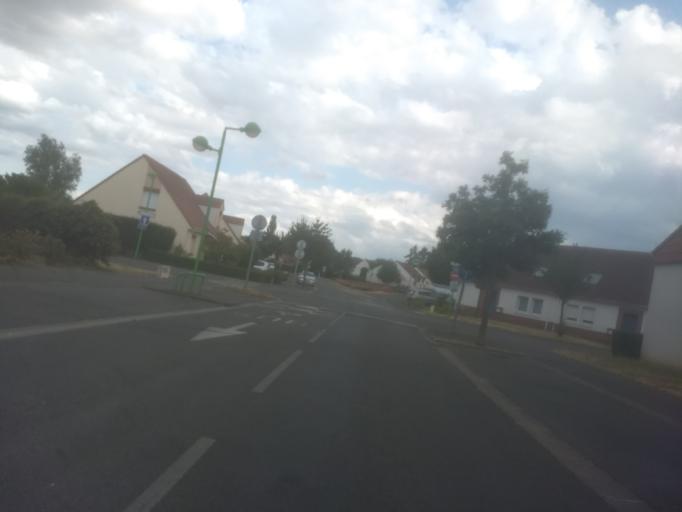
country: FR
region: Nord-Pas-de-Calais
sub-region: Departement du Pas-de-Calais
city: Beaurains
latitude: 50.2726
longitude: 2.7786
